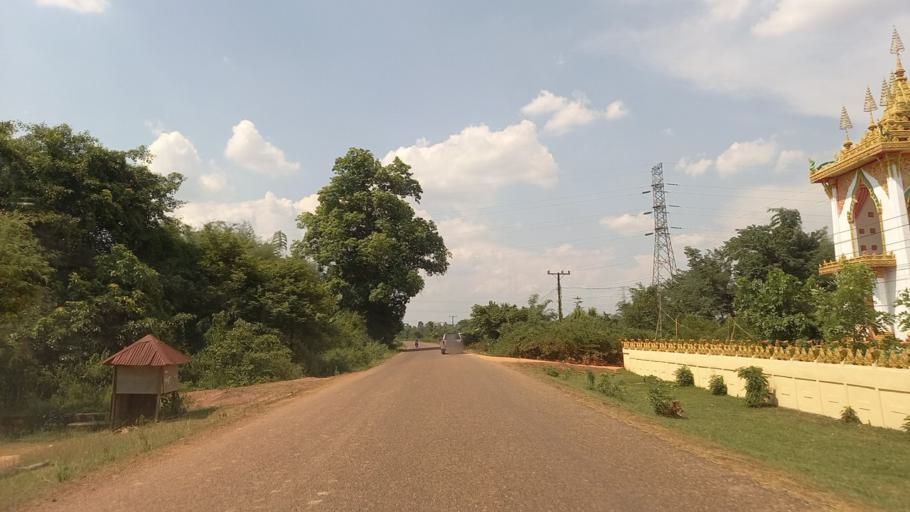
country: LA
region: Bolikhamxai
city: Muang Pakxan
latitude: 18.4083
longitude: 103.7017
